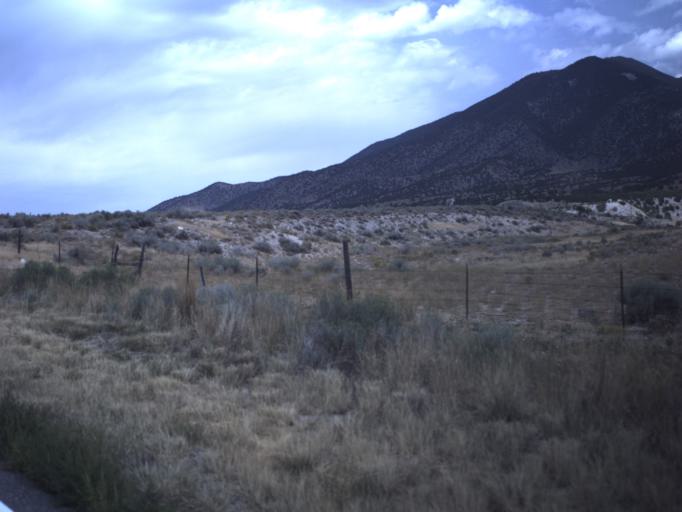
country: US
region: Utah
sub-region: Tooele County
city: Tooele
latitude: 40.3471
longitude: -112.3074
